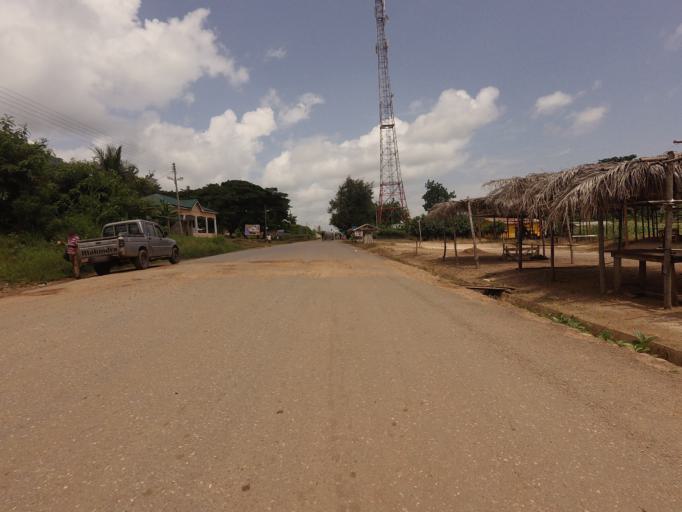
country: GH
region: Volta
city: Ho
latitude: 6.7571
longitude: 0.3601
